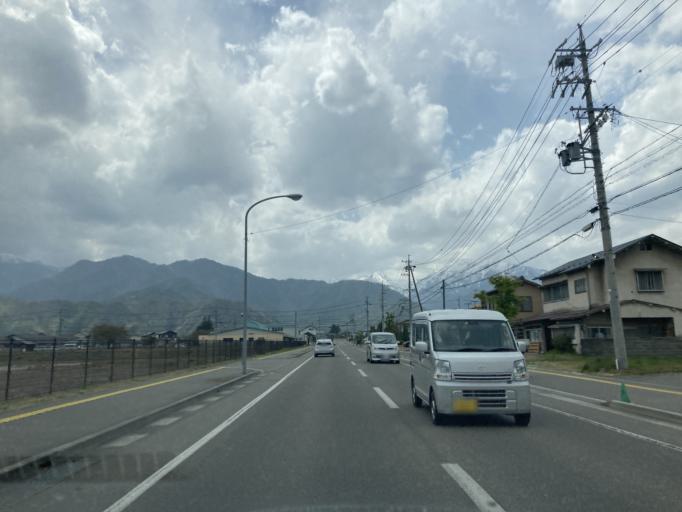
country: JP
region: Nagano
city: Omachi
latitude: 36.4991
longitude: 137.8556
